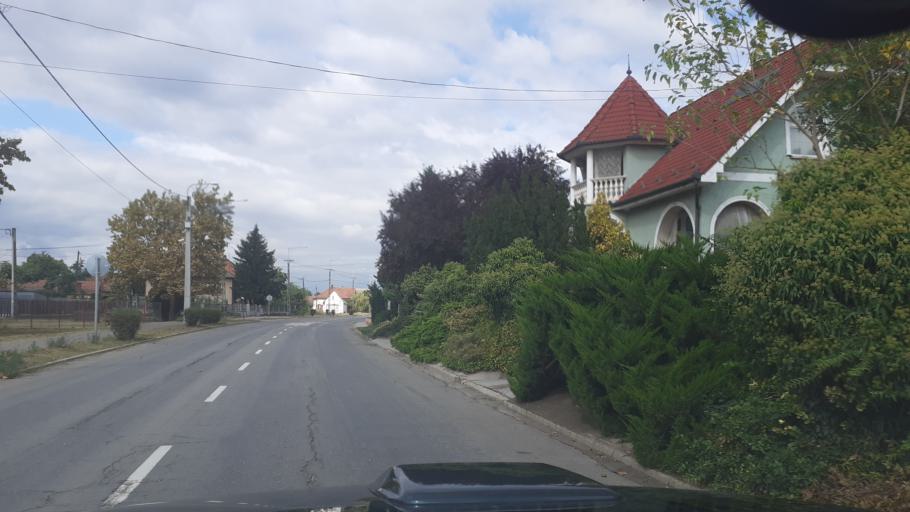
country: HU
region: Bacs-Kiskun
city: Dunavecse
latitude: 46.9096
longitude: 18.9724
